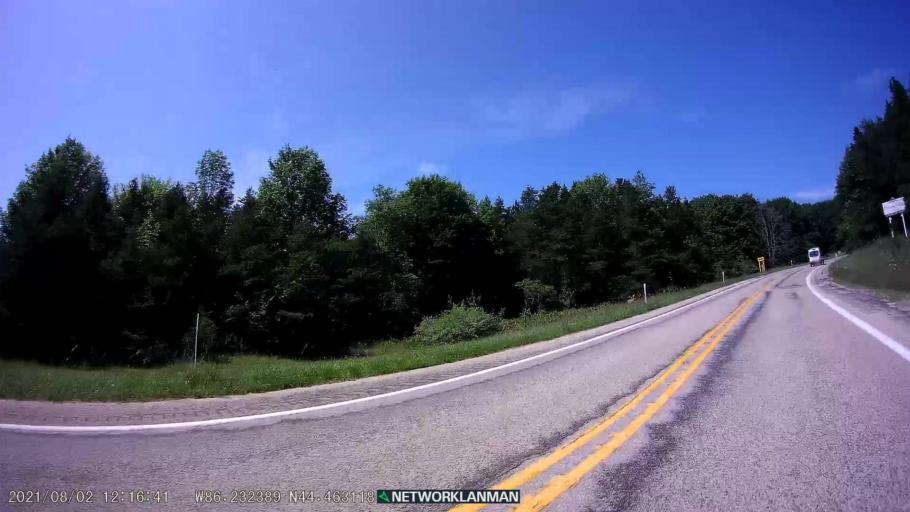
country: US
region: Michigan
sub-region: Benzie County
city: Frankfort
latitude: 44.4634
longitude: -86.2329
